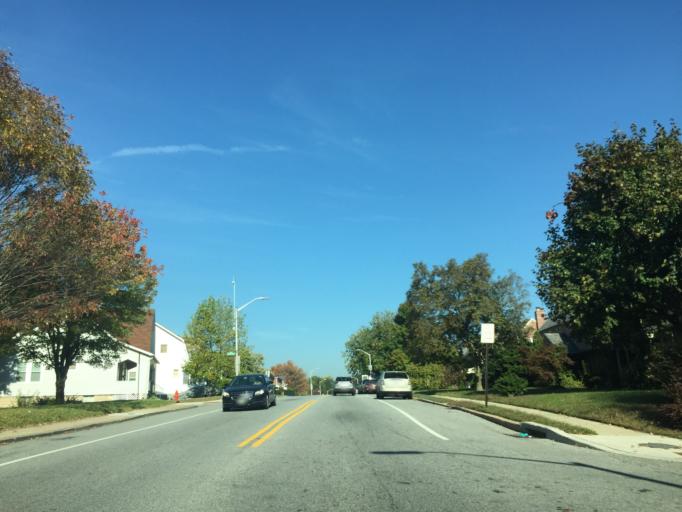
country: US
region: Maryland
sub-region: Baltimore County
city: Parkville
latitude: 39.3421
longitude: -76.5556
